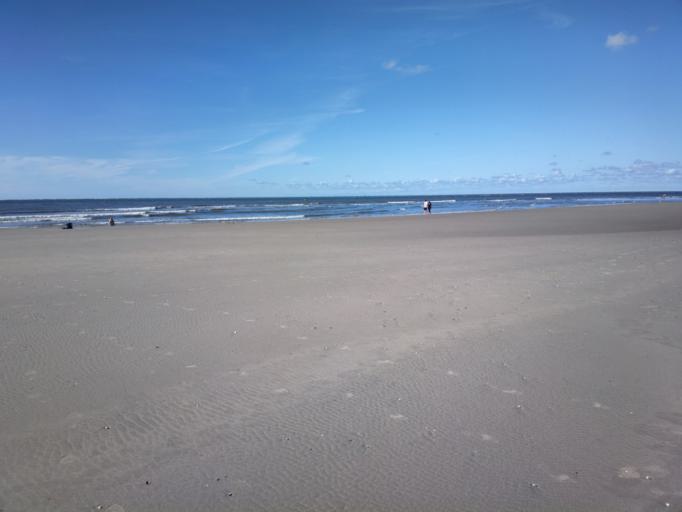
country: NL
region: North Holland
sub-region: Gemeente Texel
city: Den Burg
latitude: 53.1833
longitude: 4.8419
